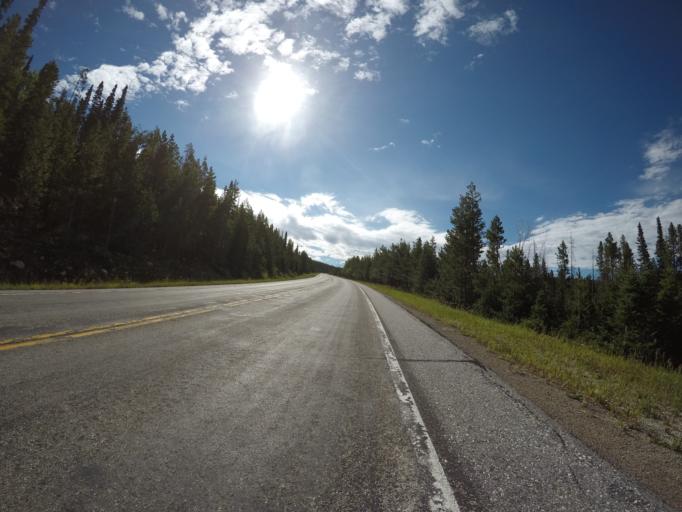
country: US
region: Wyoming
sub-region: Carbon County
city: Saratoga
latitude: 41.3268
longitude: -106.4714
